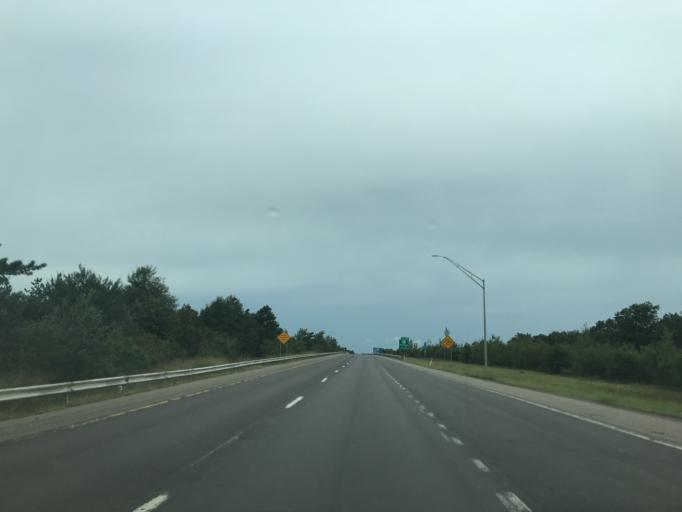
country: US
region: Pennsylvania
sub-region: Schuylkill County
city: McAdoo
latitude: 40.9307
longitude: -76.0136
